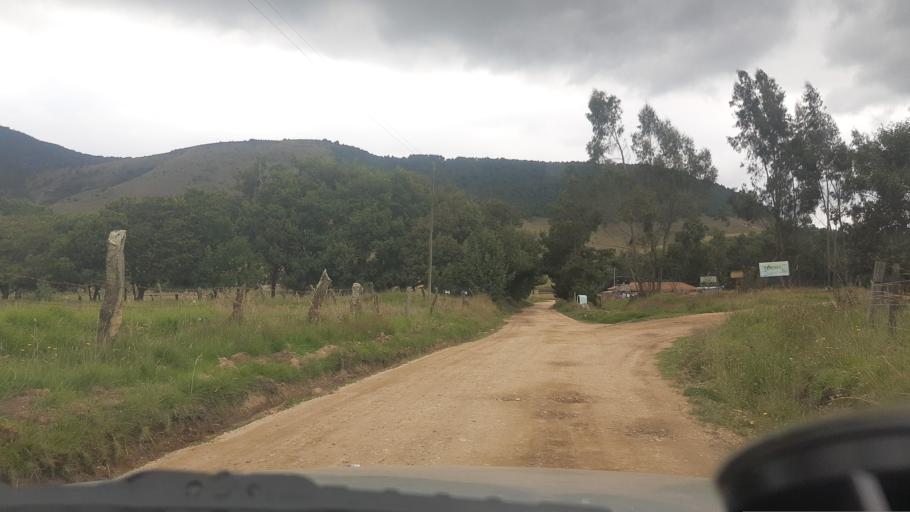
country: CO
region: Cundinamarca
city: Suesca
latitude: 5.1537
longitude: -73.7968
